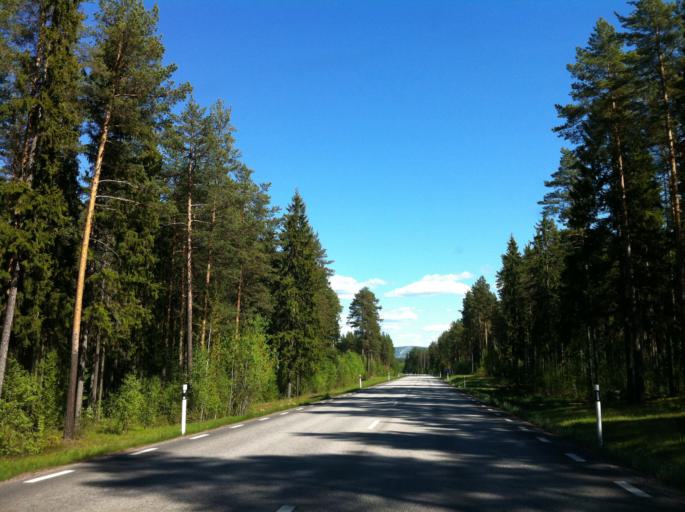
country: SE
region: Dalarna
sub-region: Rattviks Kommun
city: Vikarbyn
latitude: 60.9063
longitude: 14.9369
